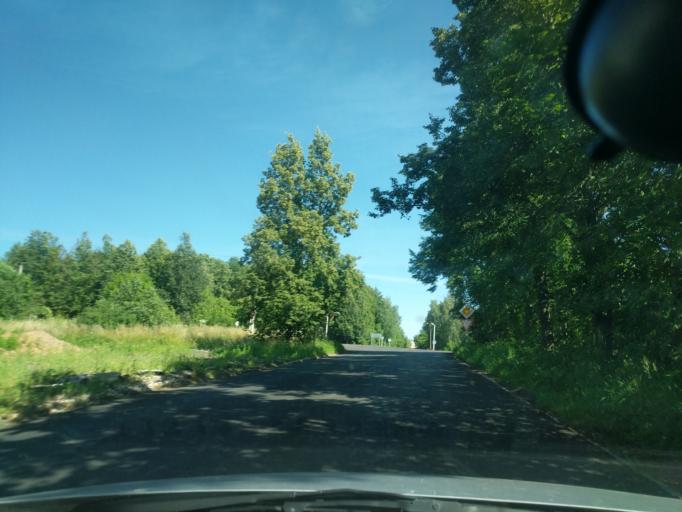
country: RU
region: Moskovskaya
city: Pushchino
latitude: 54.8315
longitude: 37.5988
